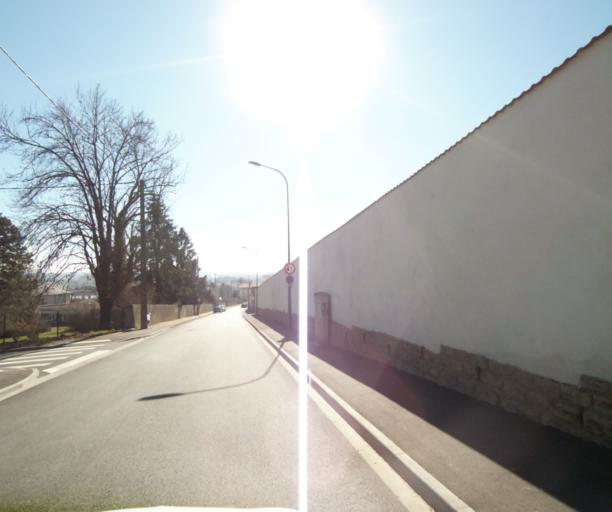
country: FR
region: Lorraine
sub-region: Departement de Meurthe-et-Moselle
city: Saint-Max
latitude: 48.7089
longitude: 6.2155
